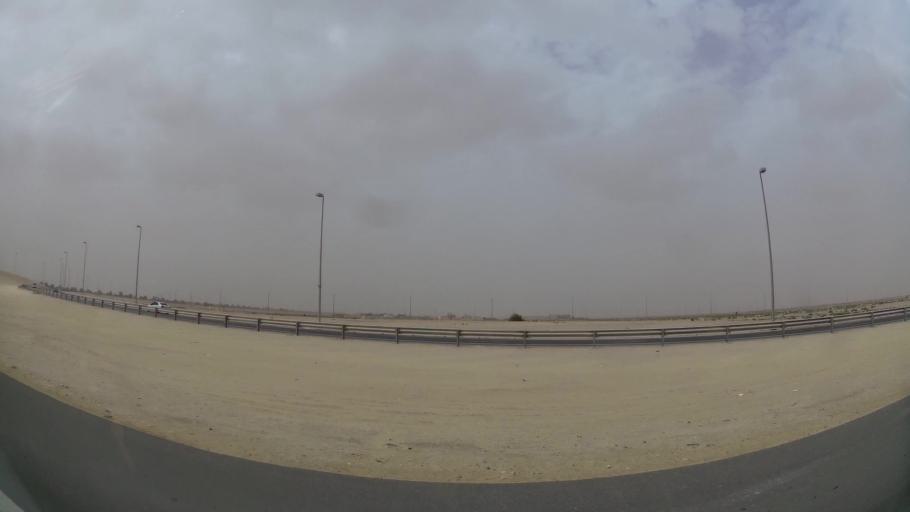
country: AE
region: Abu Dhabi
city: Abu Dhabi
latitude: 24.4198
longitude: 54.7136
